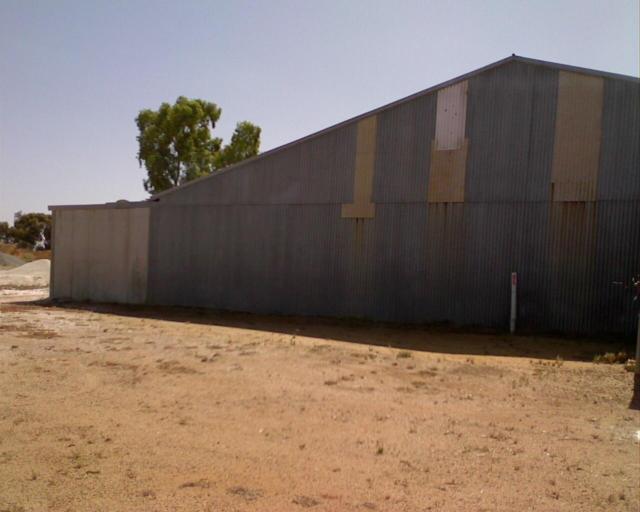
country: AU
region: Western Australia
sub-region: Merredin
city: Merredin
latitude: -30.9127
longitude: 118.2067
